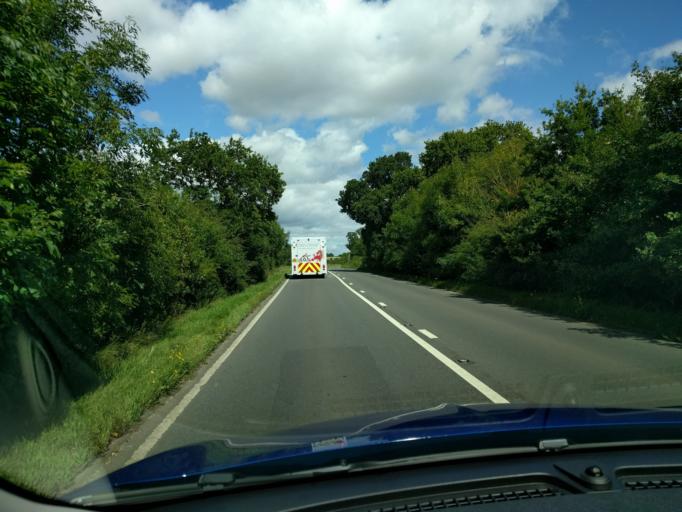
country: GB
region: England
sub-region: Warwickshire
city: Stratford-upon-Avon
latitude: 52.1574
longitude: -1.7305
